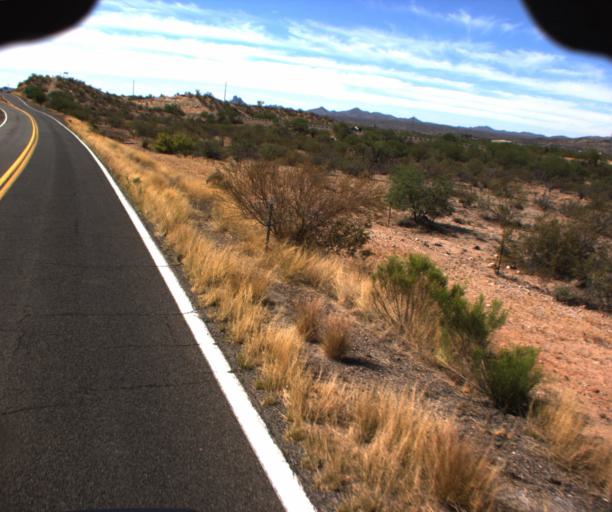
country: US
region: Arizona
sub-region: Maricopa County
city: Wickenburg
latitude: 34.0290
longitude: -112.8110
